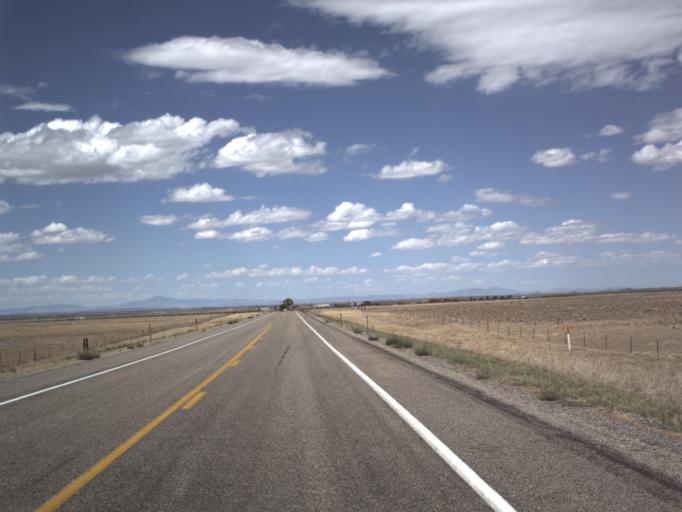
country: US
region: Utah
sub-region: Millard County
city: Fillmore
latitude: 39.1145
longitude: -112.3061
